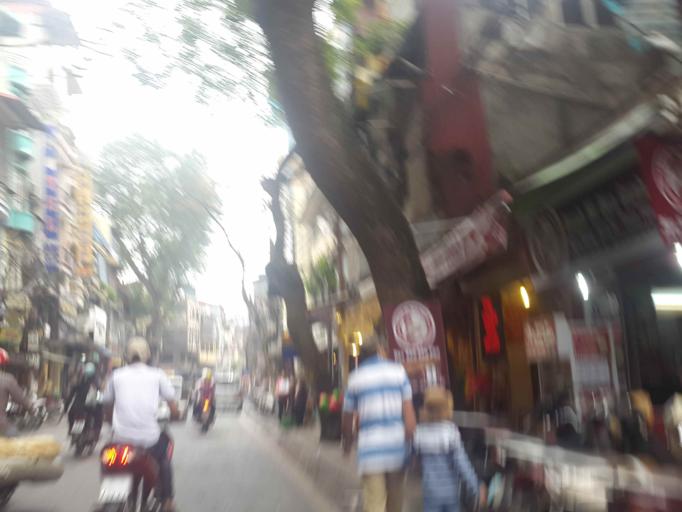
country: VN
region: Ha Noi
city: Hoan Kiem
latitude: 21.0375
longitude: 105.8481
